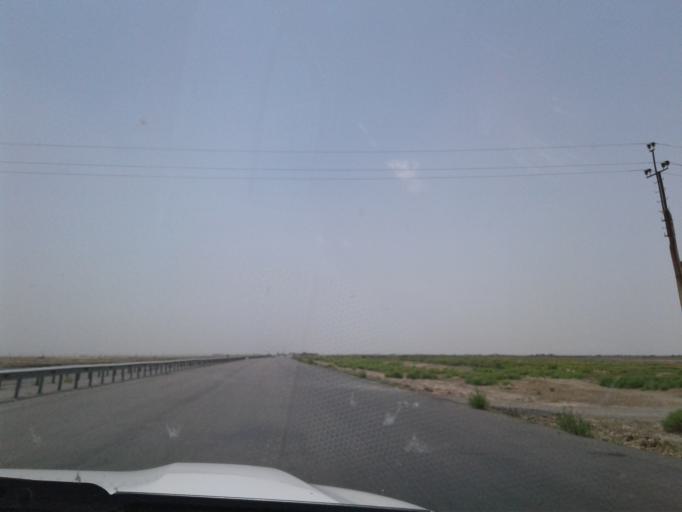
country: TM
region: Ahal
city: Tejen
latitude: 37.3309
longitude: 60.3674
